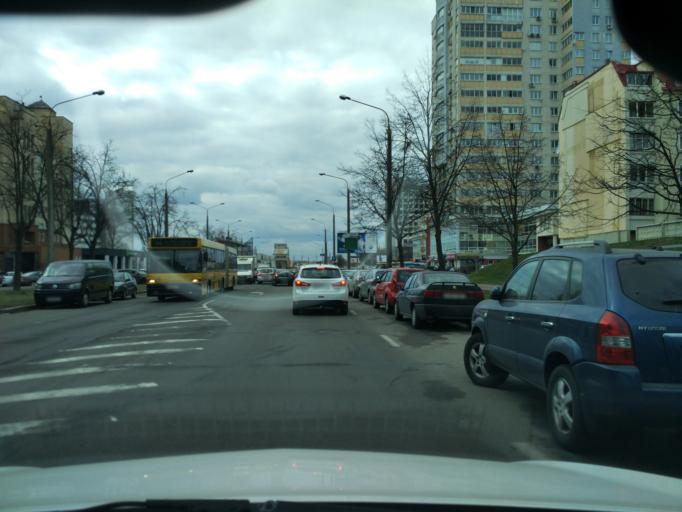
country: BY
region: Minsk
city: Minsk
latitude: 53.9346
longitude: 27.5850
